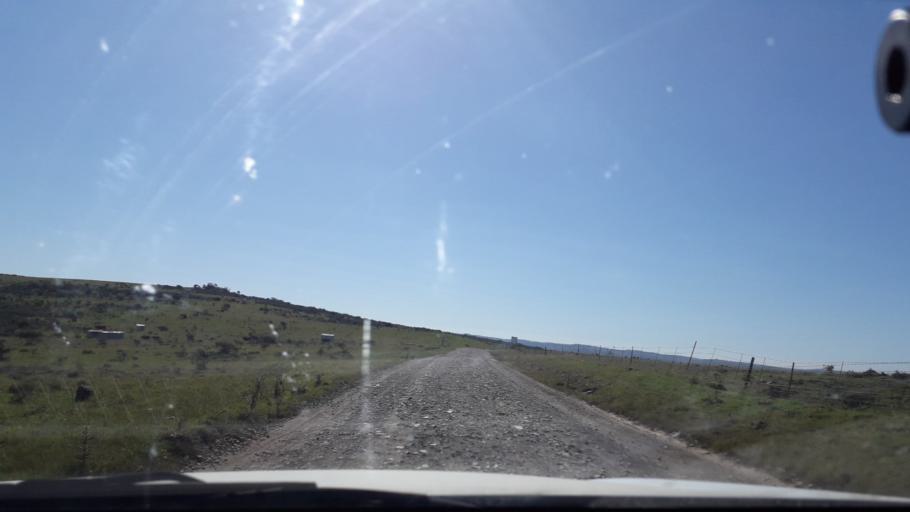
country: ZA
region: Eastern Cape
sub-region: Amathole District Municipality
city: Komga
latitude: -32.7939
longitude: 27.9513
